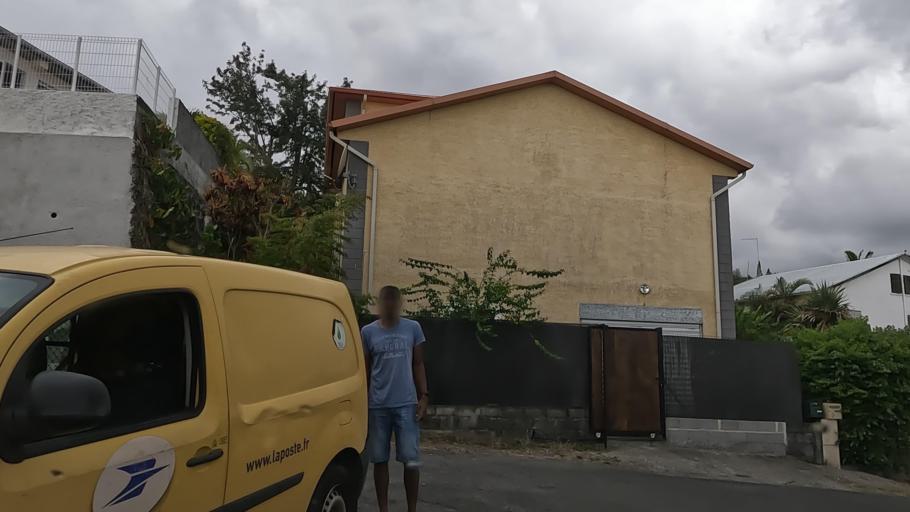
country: RE
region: Reunion
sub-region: Reunion
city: Le Tampon
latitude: -21.2740
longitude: 55.5023
